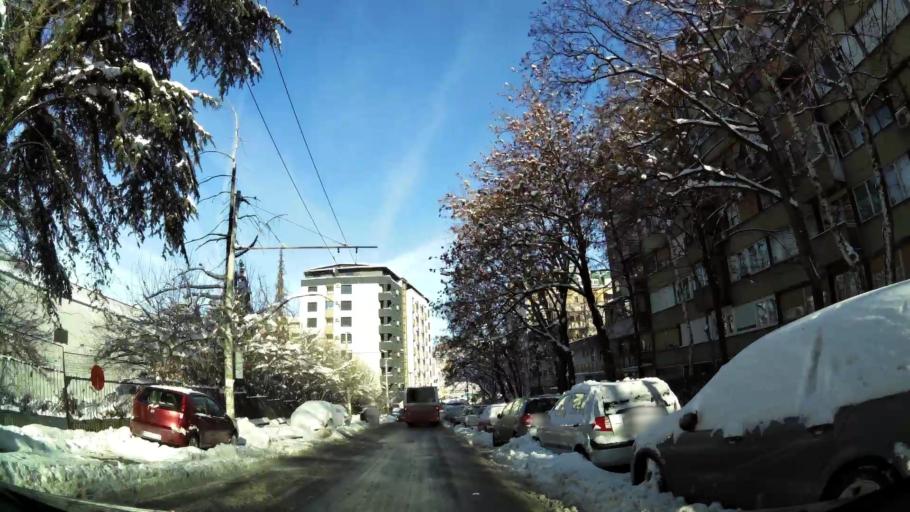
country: RS
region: Central Serbia
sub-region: Belgrade
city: Palilula
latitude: 44.7871
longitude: 20.5059
